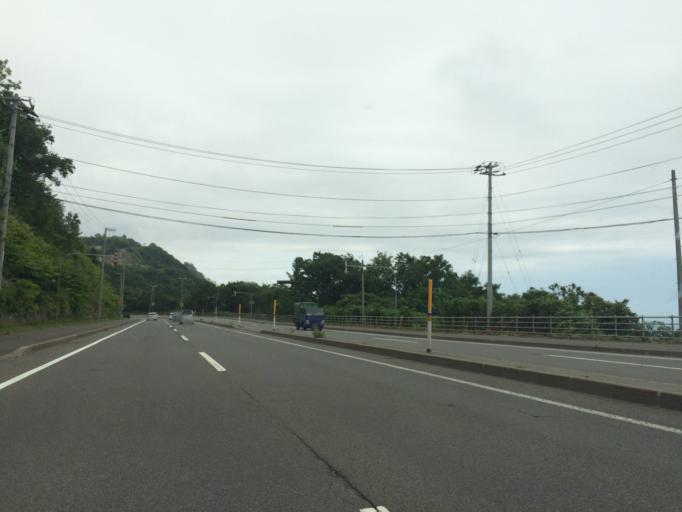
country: JP
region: Hokkaido
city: Otaru
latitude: 43.1617
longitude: 141.1072
